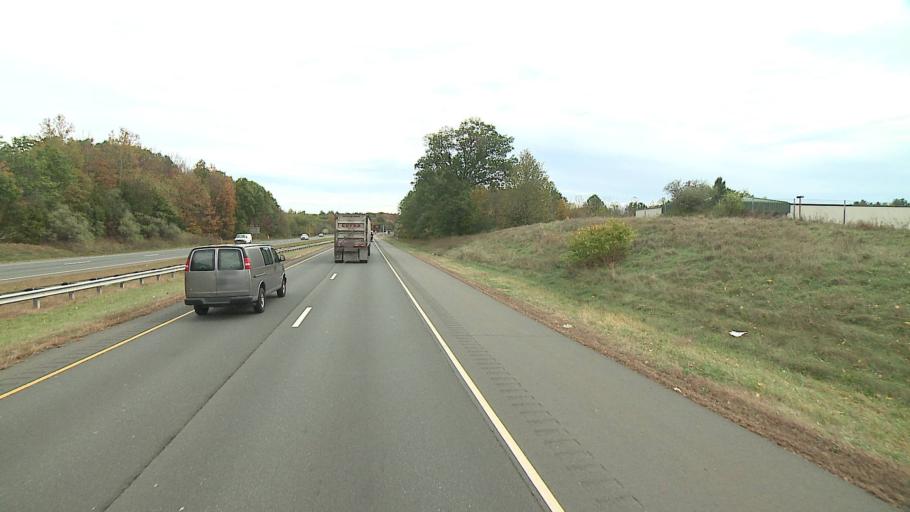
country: US
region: Connecticut
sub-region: Hartford County
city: Kensington
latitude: 41.6236
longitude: -72.7222
